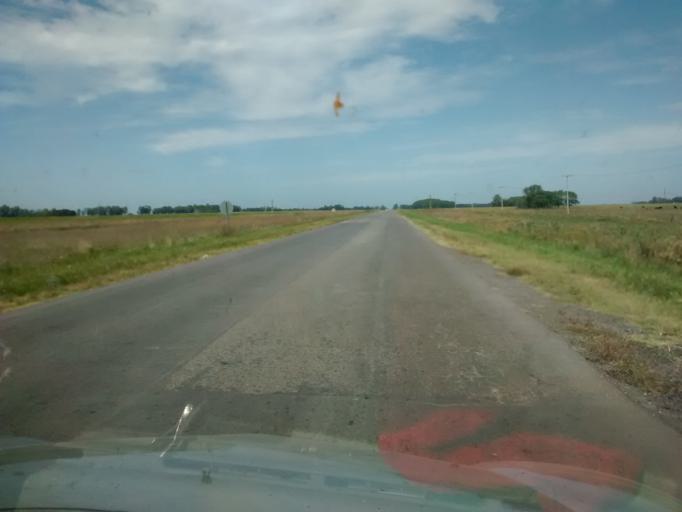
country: AR
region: Buenos Aires
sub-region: Partido de Ayacucho
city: Ayacucho
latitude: -37.1868
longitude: -58.5121
